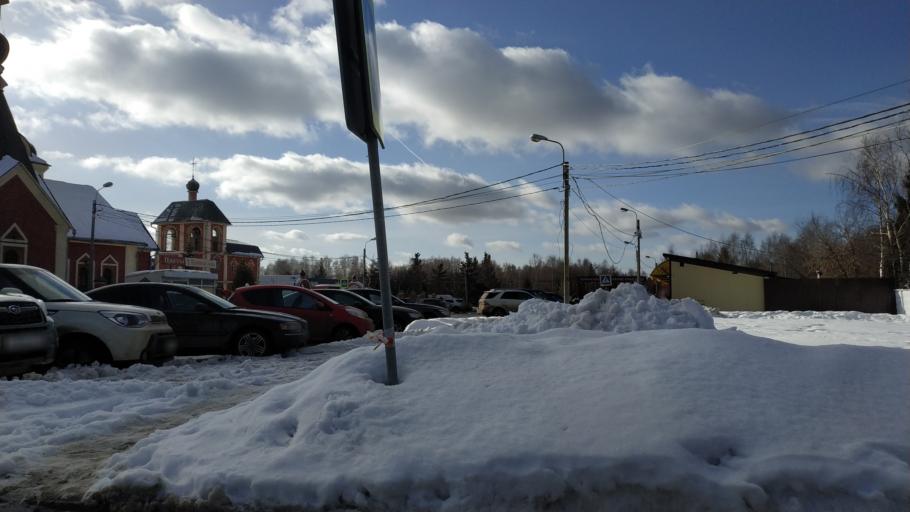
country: RU
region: Moskovskaya
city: Mosrentgen
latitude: 55.6073
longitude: 37.4486
